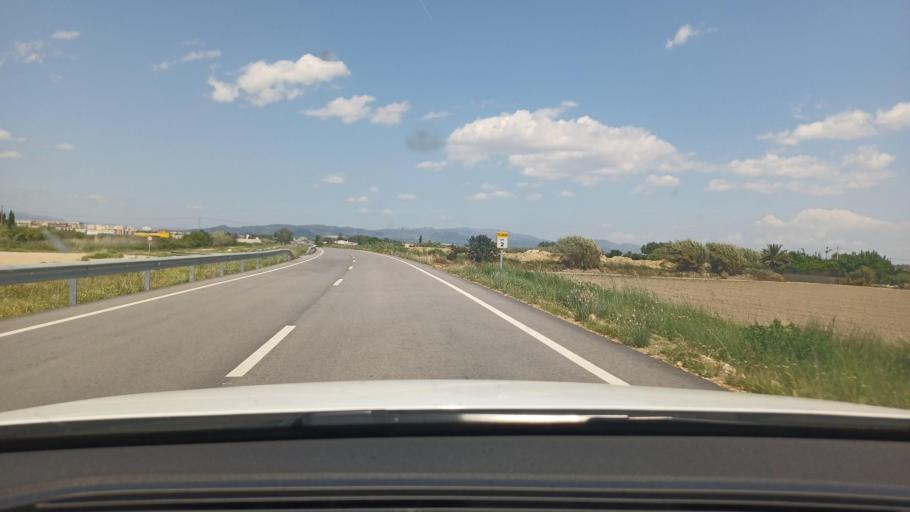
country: ES
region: Catalonia
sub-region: Provincia de Tarragona
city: Amposta
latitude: 40.6908
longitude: 0.5904
